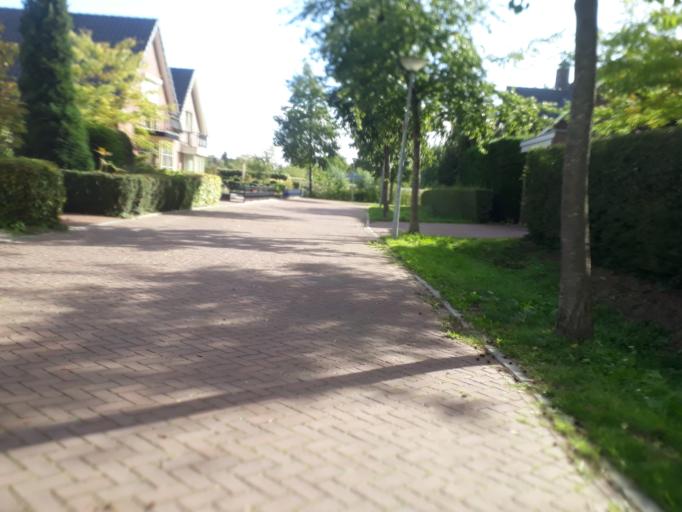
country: NL
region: Gelderland
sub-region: Gemeente Zevenaar
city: Zevenaar
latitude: 51.9231
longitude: 6.0614
